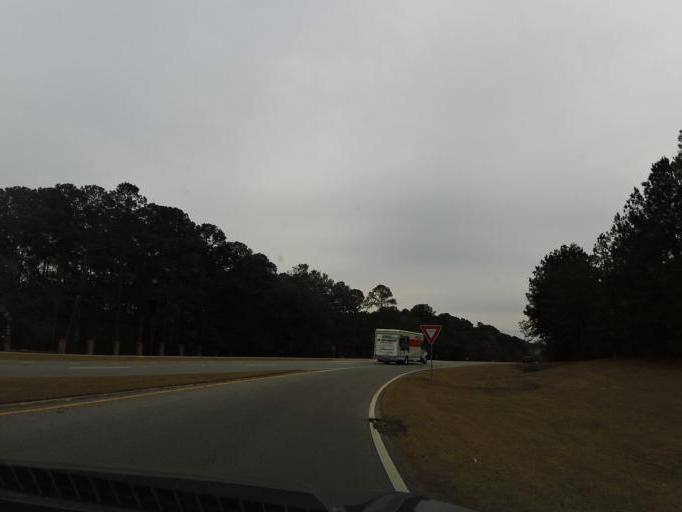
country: US
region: Georgia
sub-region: Thomas County
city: Thomasville
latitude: 30.8110
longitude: -83.9391
